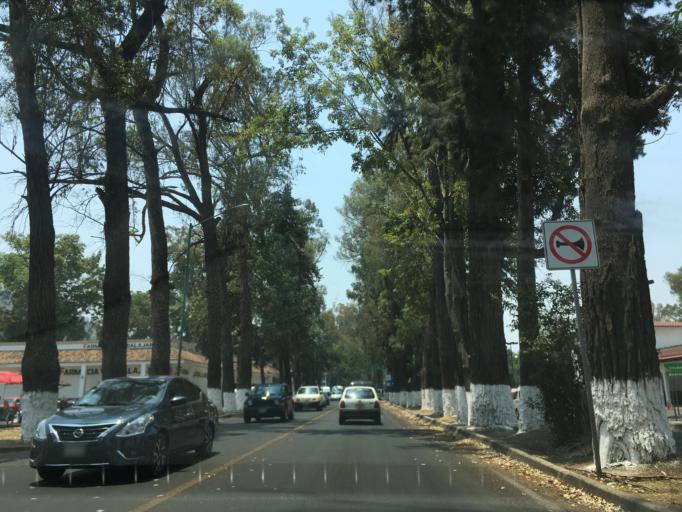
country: MX
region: Michoacan
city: Patzcuaro
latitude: 19.5313
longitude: -101.6112
